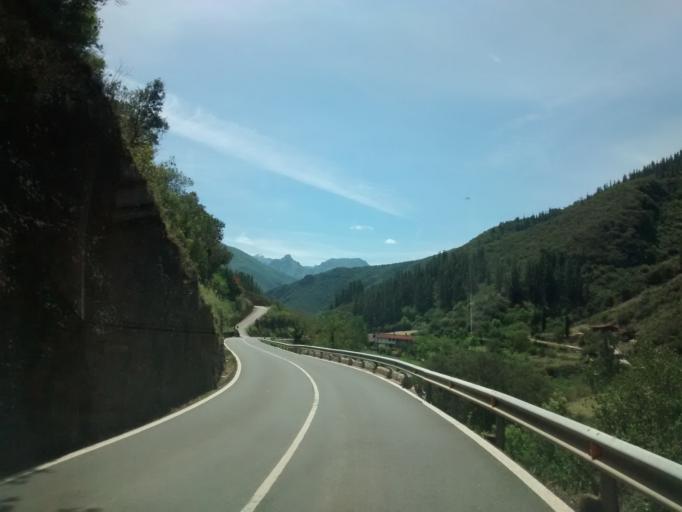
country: ES
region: Cantabria
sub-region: Provincia de Cantabria
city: Potes
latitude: 43.1472
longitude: -4.6271
